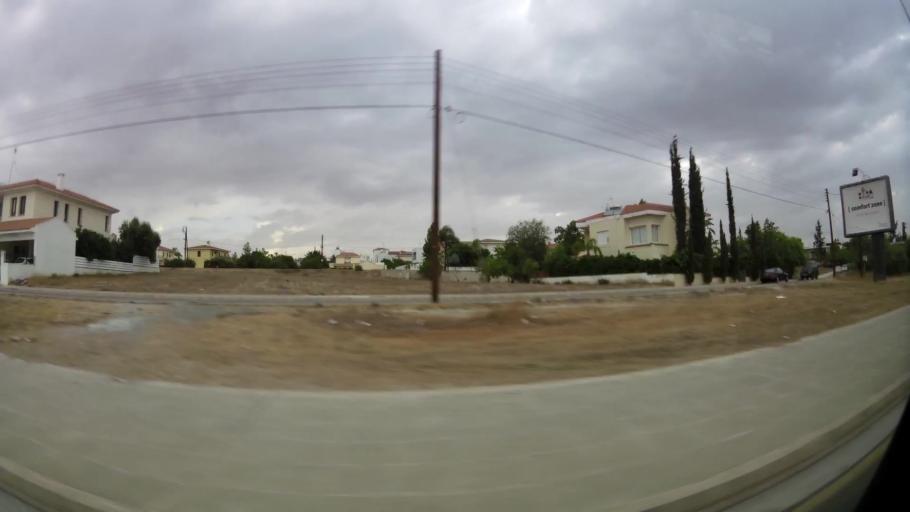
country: CY
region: Lefkosia
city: Nicosia
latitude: 35.1381
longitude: 33.3578
